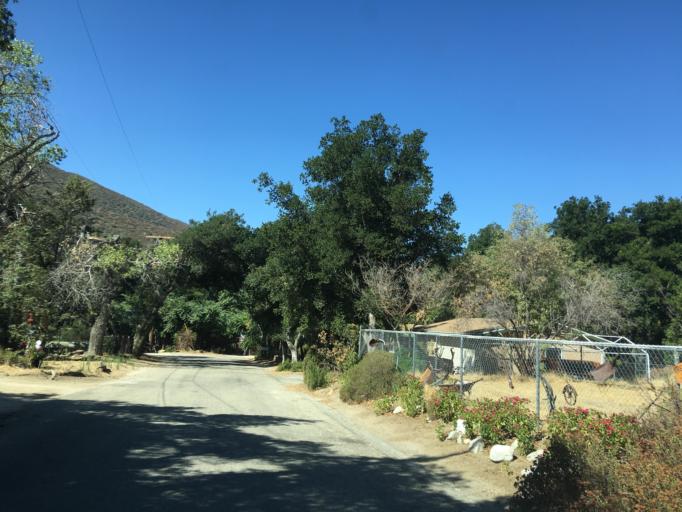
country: US
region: California
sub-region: Los Angeles County
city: Green Valley
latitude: 34.6178
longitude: -118.4162
